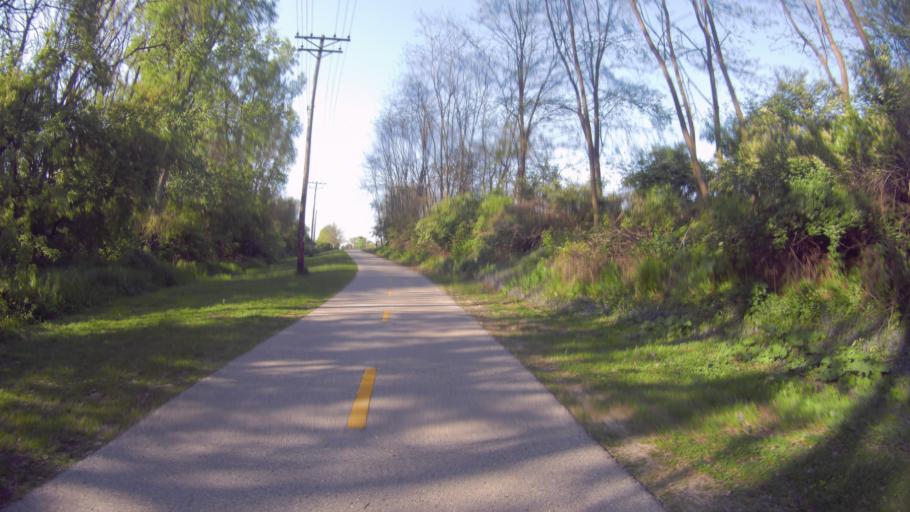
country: US
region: Wisconsin
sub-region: Dane County
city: Shorewood Hills
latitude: 43.0251
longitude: -89.4612
